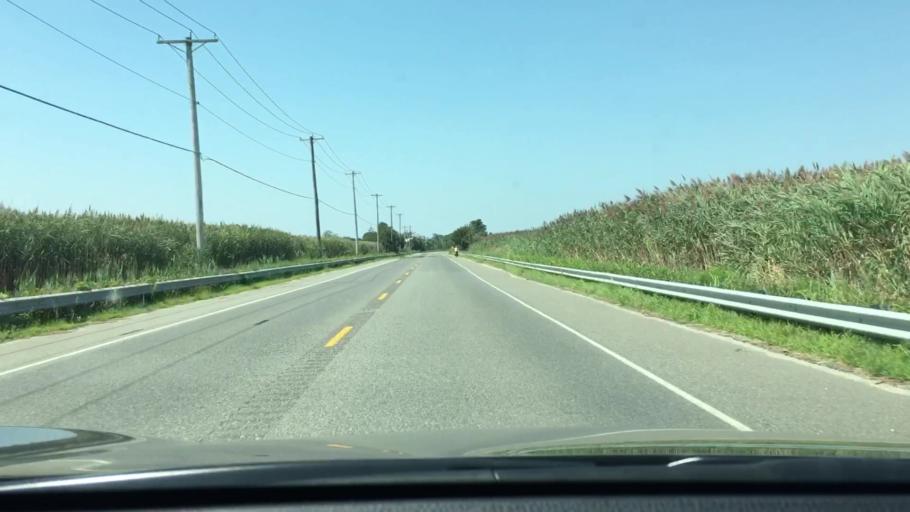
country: US
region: New Jersey
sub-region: Cumberland County
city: Port Norris
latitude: 39.2876
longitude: -74.9812
